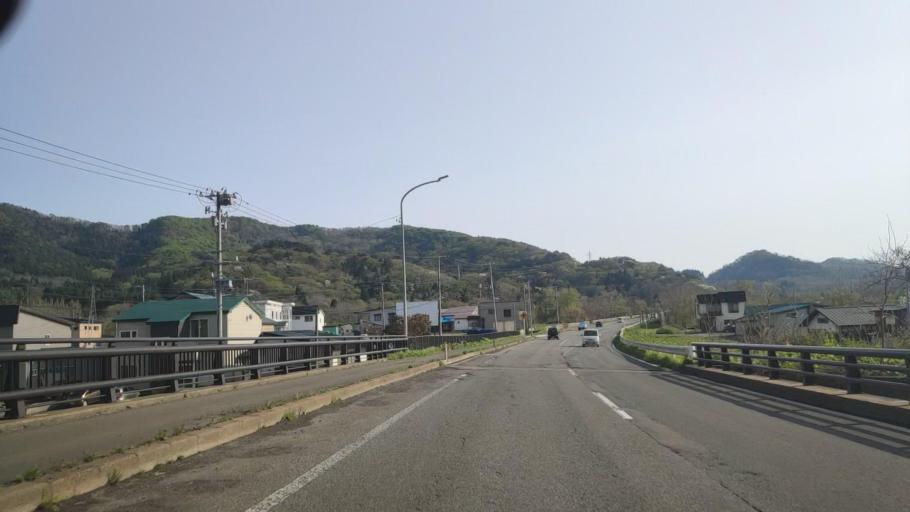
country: JP
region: Aomori
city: Aomori Shi
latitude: 40.8725
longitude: 140.8512
